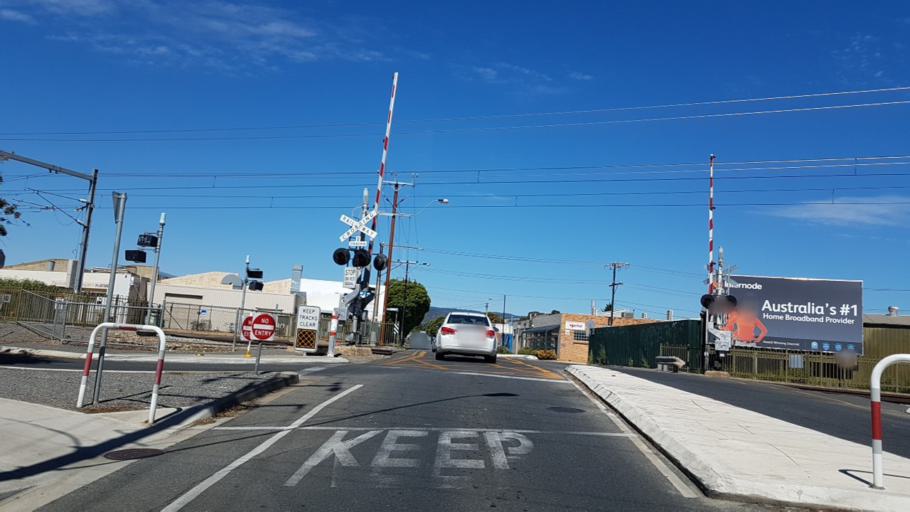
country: AU
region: South Australia
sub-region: Mitcham
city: Clarence Gardens
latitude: -34.9798
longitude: 138.5687
